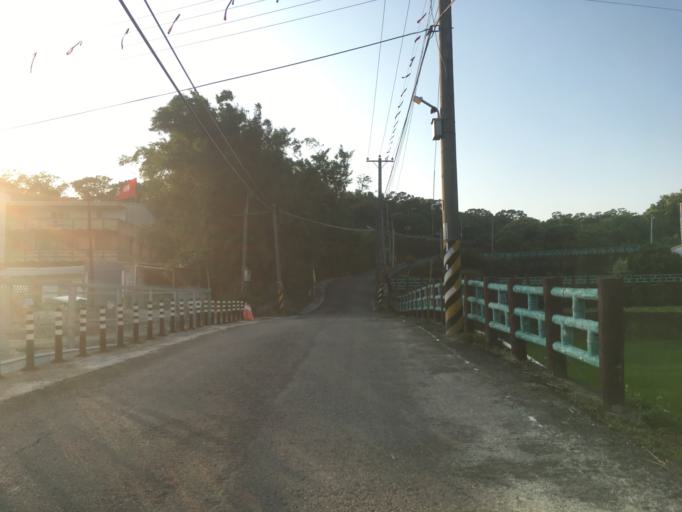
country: TW
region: Taiwan
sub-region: Hsinchu
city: Hsinchu
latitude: 24.7607
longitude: 120.9625
